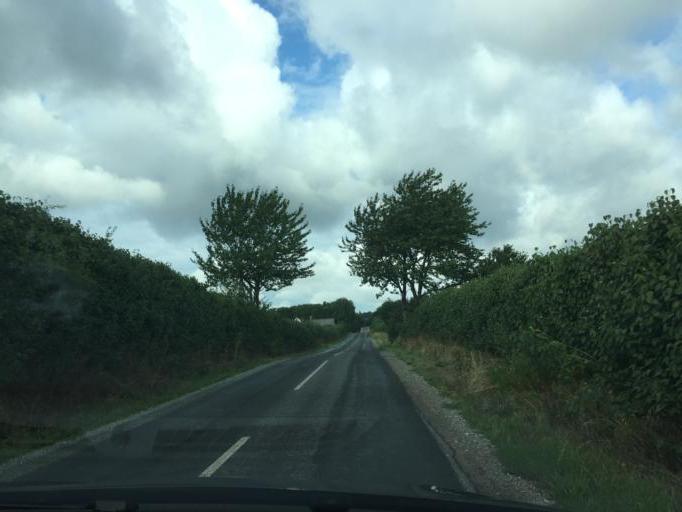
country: DK
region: South Denmark
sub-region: Assens Kommune
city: Harby
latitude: 55.1939
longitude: 10.2153
